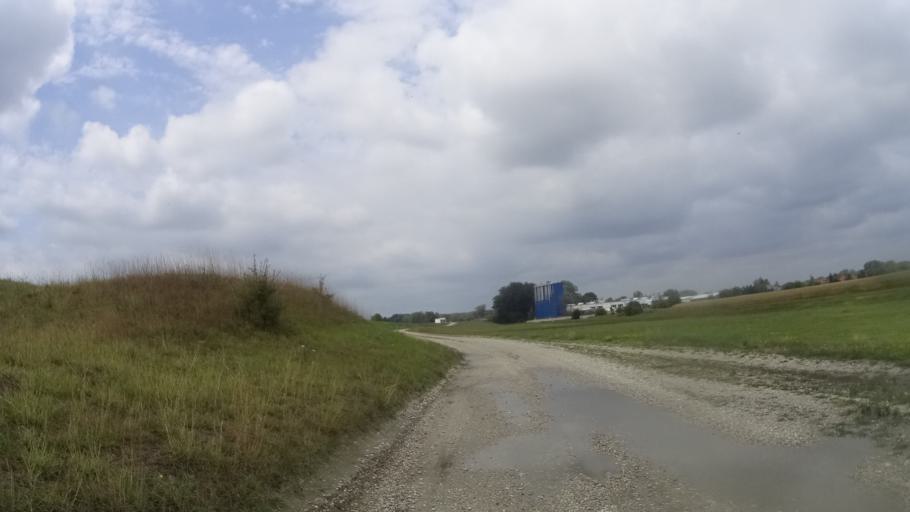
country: HU
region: Gyor-Moson-Sopron
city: Bony
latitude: 47.7438
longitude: 17.8835
